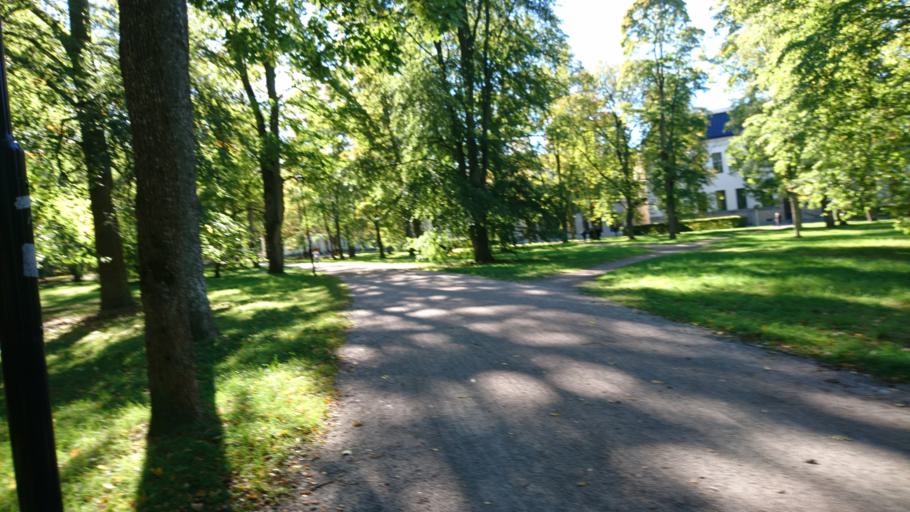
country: SE
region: Uppsala
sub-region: Uppsala Kommun
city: Uppsala
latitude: 59.8550
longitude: 17.6285
